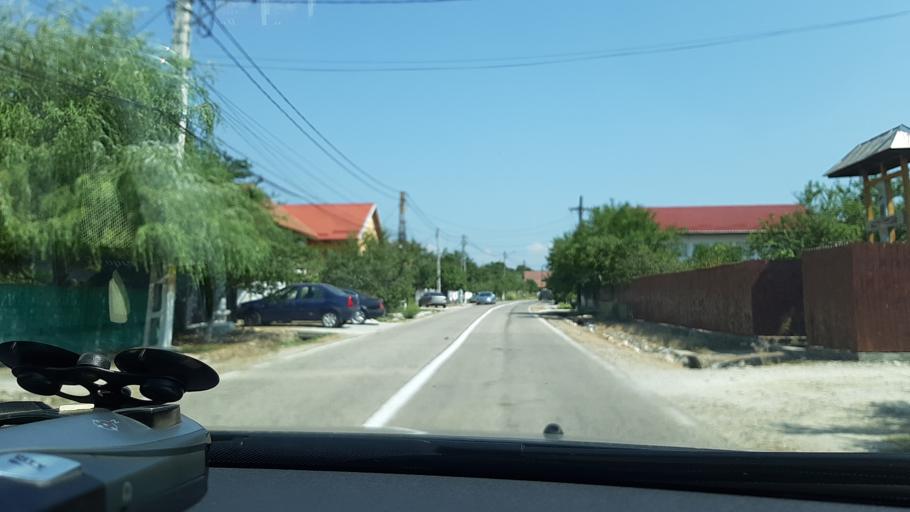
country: RO
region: Gorj
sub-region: Comuna Targu Carbunesti
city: Targu Carbunesti
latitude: 44.9473
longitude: 23.5399
